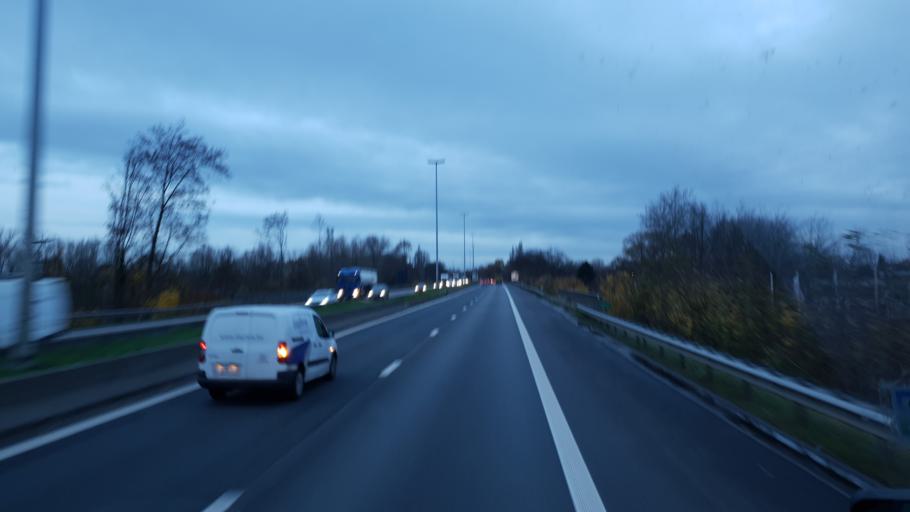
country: BE
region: Flanders
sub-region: Provincie Oost-Vlaanderen
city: Destelbergen
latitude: 51.0680
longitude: 3.8090
